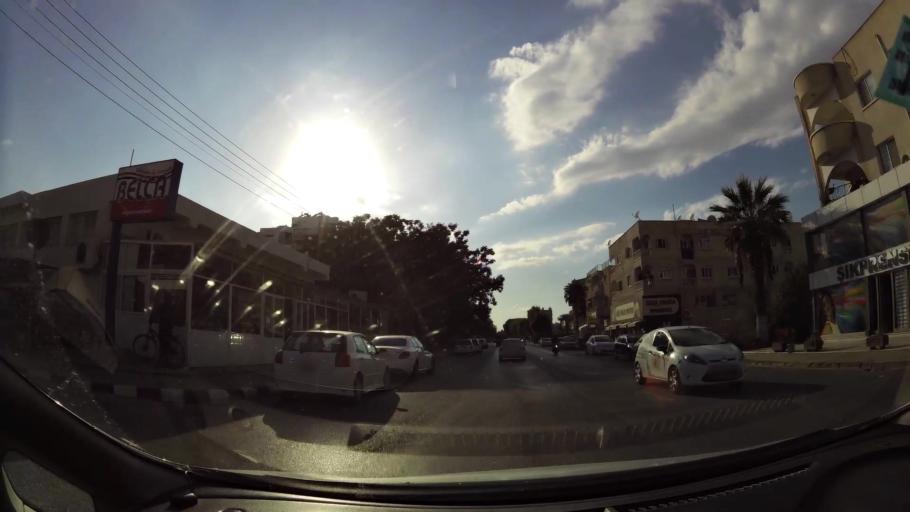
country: CY
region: Lefkosia
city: Nicosia
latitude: 35.1903
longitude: 33.3649
